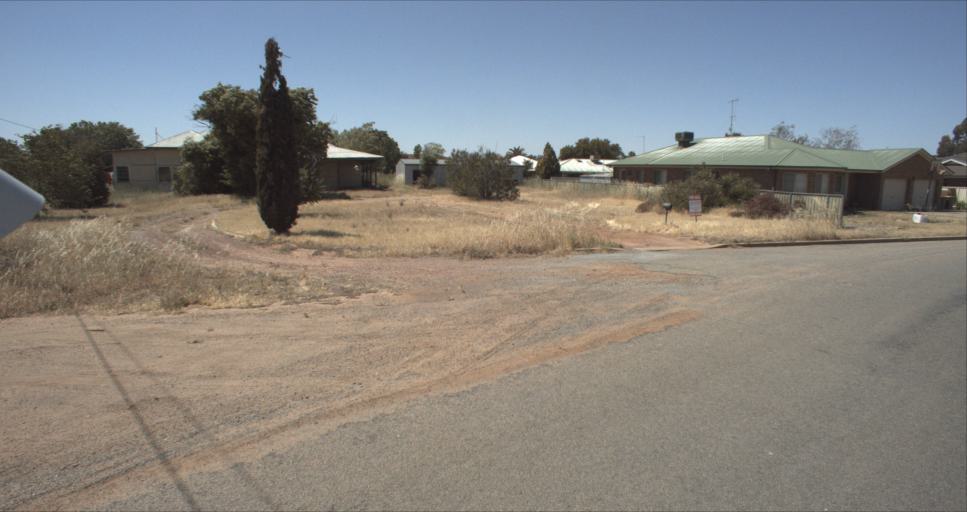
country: AU
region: New South Wales
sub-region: Leeton
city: Leeton
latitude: -34.5442
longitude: 146.3964
